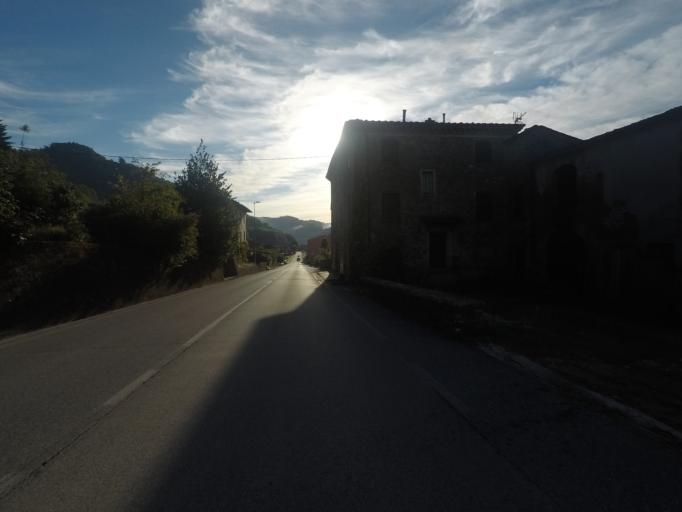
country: IT
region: Tuscany
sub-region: Provincia di Lucca
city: Pescaglia
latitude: 43.9522
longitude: 10.4330
